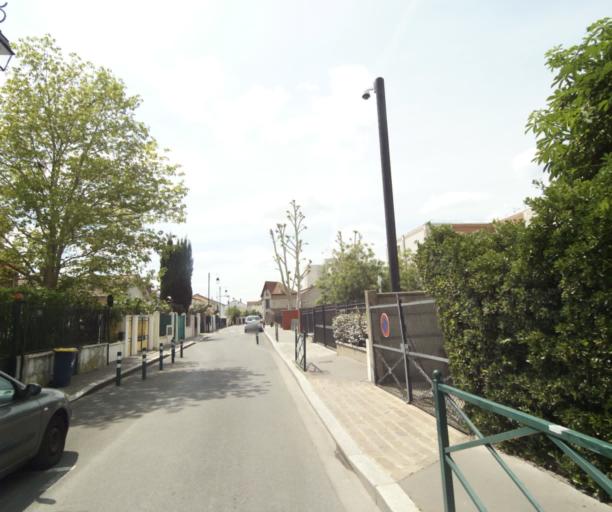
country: FR
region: Ile-de-France
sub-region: Departement du Val-d'Oise
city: Bezons
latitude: 48.9205
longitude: 2.2318
